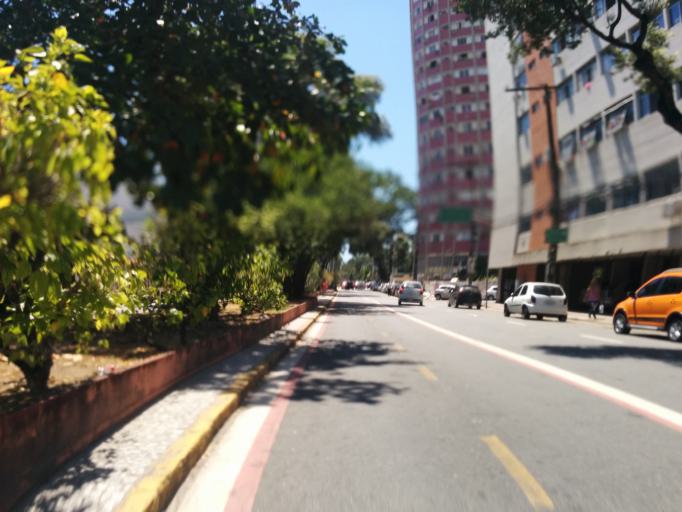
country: BR
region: Pernambuco
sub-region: Recife
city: Recife
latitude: -8.0531
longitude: -34.8830
